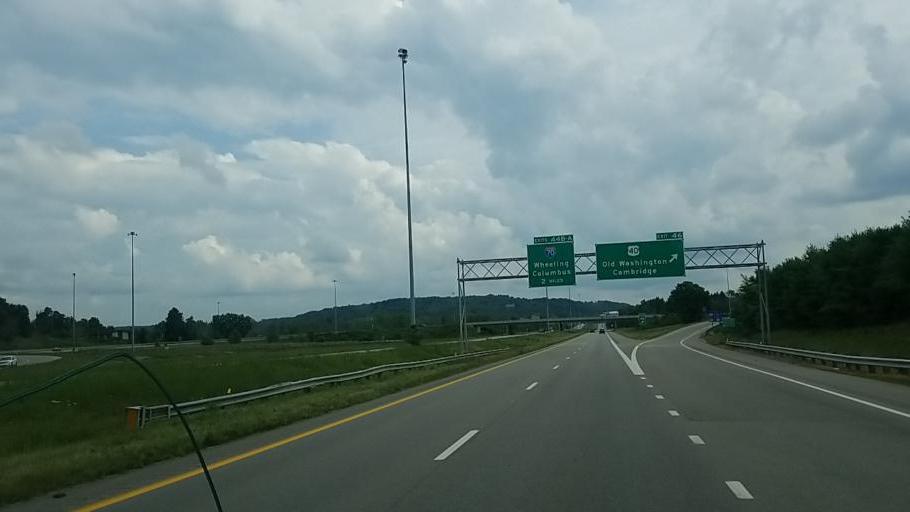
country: US
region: Ohio
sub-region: Guernsey County
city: Cambridge
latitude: 40.0311
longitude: -81.5621
